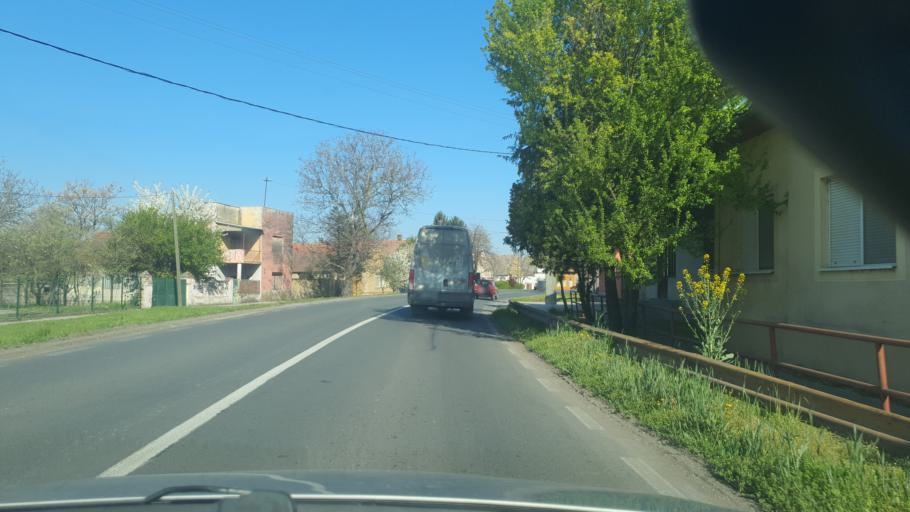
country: RS
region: Autonomna Pokrajina Vojvodina
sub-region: Zapadnobacki Okrug
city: Kula
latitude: 45.6922
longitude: 19.3815
